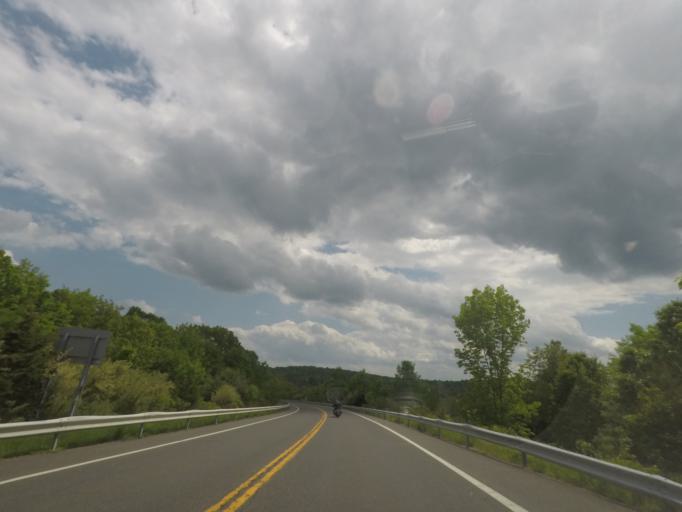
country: US
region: New York
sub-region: Dutchess County
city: Pine Plains
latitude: 42.0925
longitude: -73.6896
